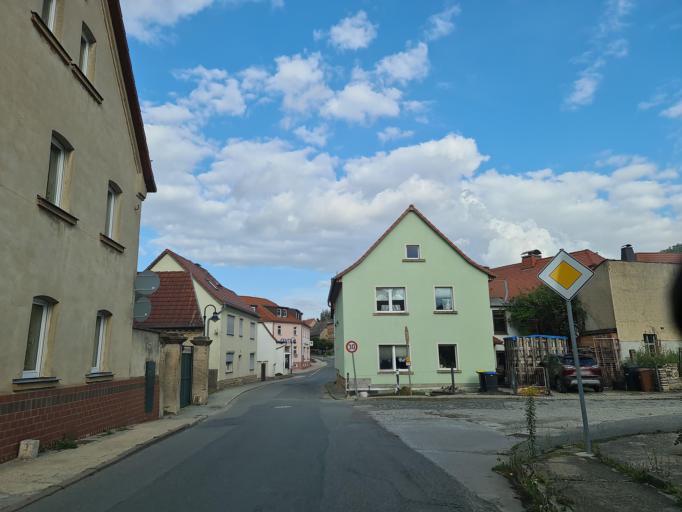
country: DE
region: Saxony-Anhalt
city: Droyssig
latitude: 51.0416
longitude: 12.0244
